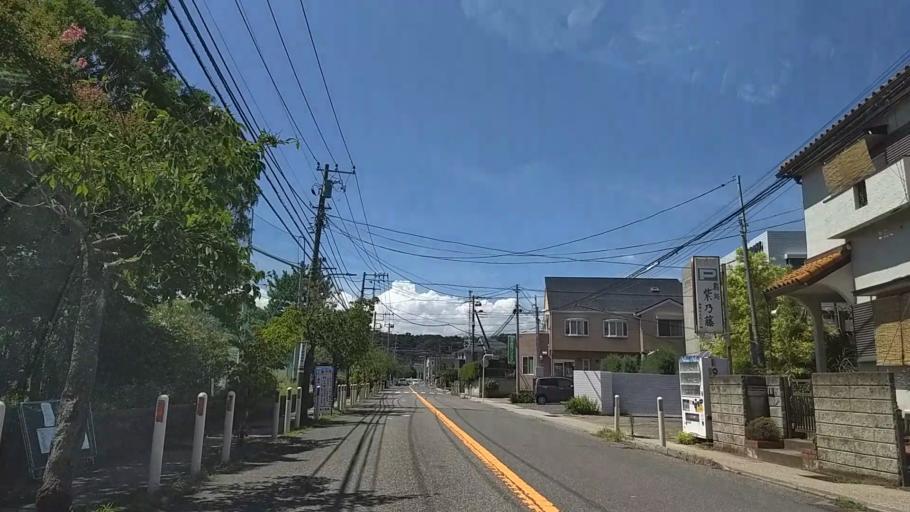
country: JP
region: Kanagawa
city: Zushi
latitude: 35.3014
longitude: 139.5932
